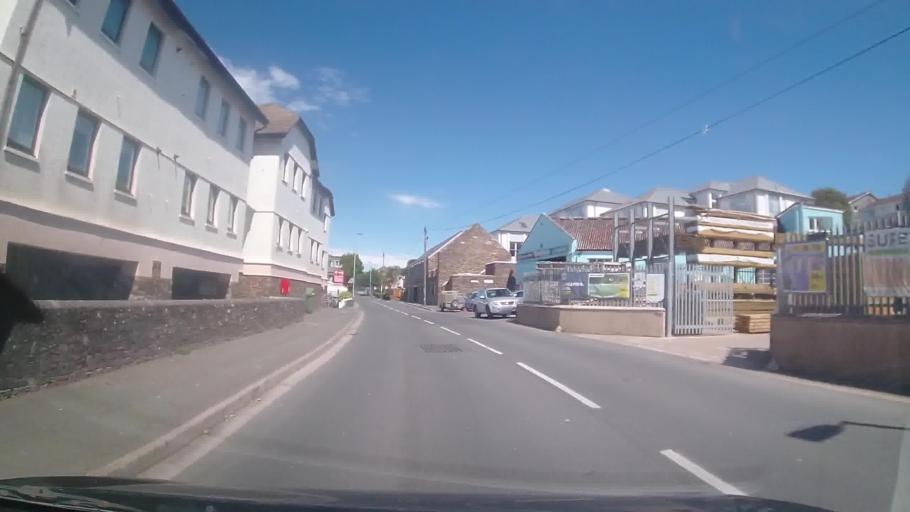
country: GB
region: England
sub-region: Devon
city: Kingsbridge
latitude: 50.2773
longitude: -3.7722
